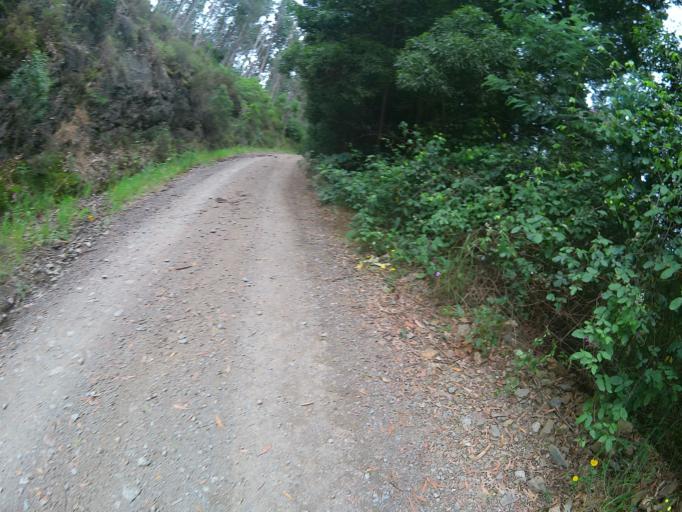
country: PT
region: Aveiro
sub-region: Albergaria-A-Velha
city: Branca
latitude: 40.7671
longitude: -8.4443
